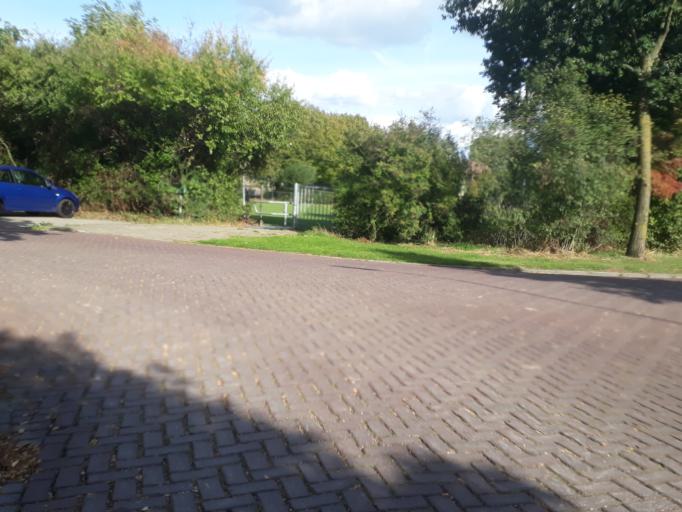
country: NL
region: Gelderland
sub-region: Gemeente Zevenaar
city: Zevenaar
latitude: 51.9356
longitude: 6.0535
